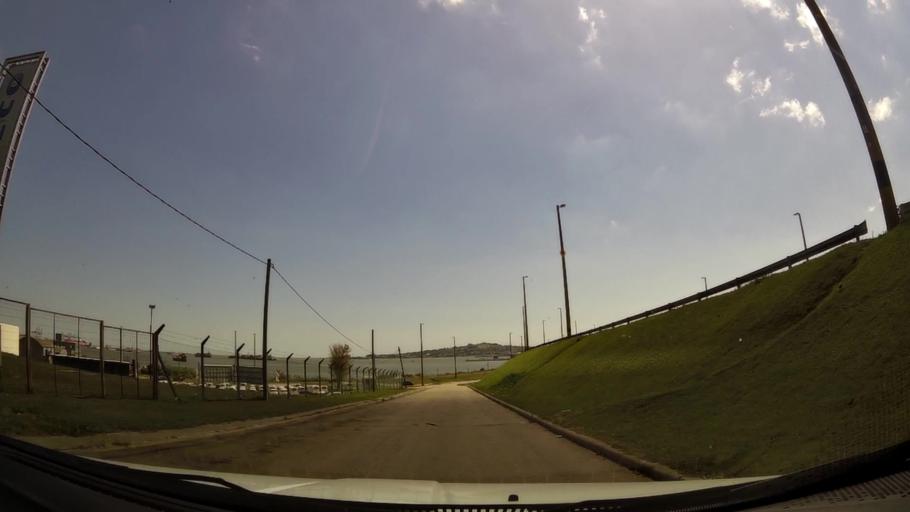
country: UY
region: Montevideo
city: Montevideo
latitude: -34.8745
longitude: -56.2094
